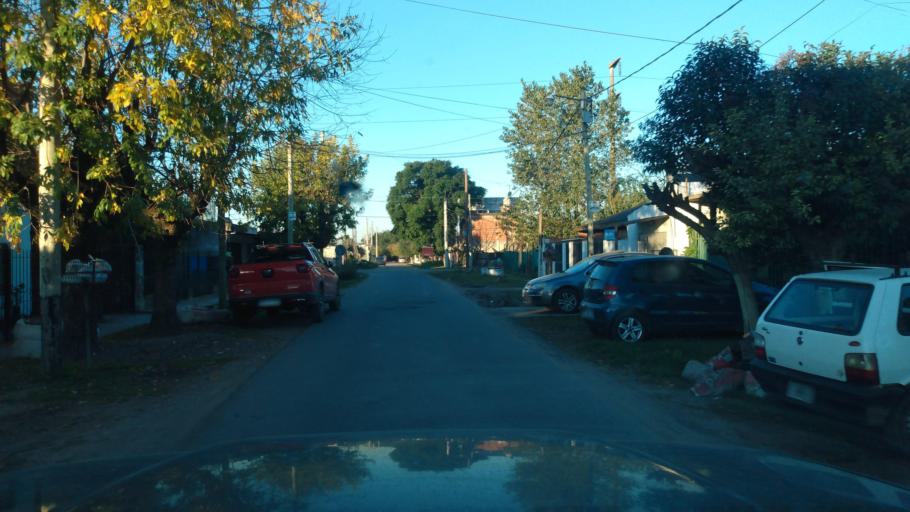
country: AR
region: Buenos Aires
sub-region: Partido de Merlo
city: Merlo
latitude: -34.6570
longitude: -58.7471
